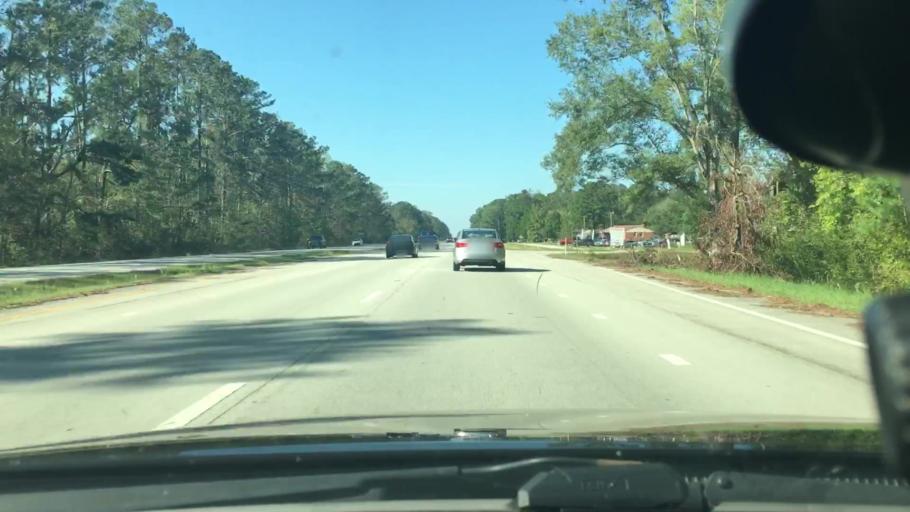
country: US
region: North Carolina
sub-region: Craven County
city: Fairfield Harbour
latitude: 35.0206
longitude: -76.9976
